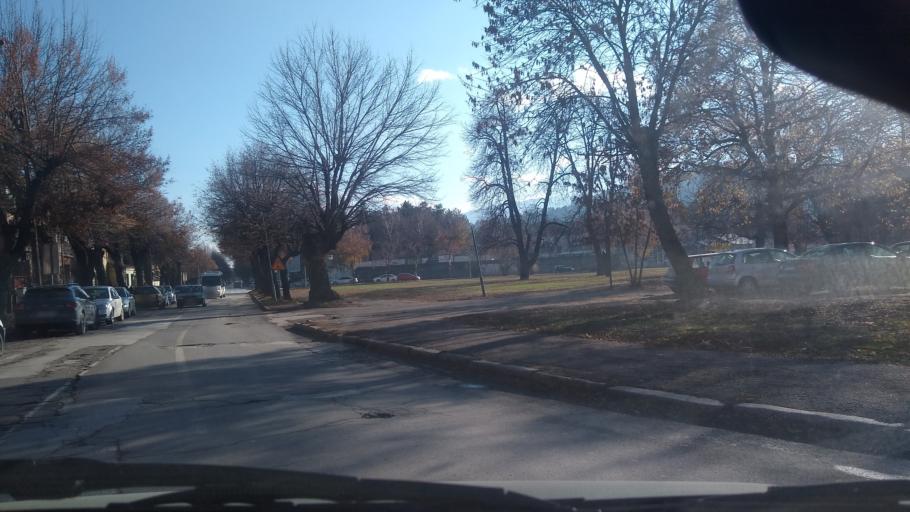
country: MK
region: Bitola
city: Bitola
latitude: 41.0246
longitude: 21.3387
